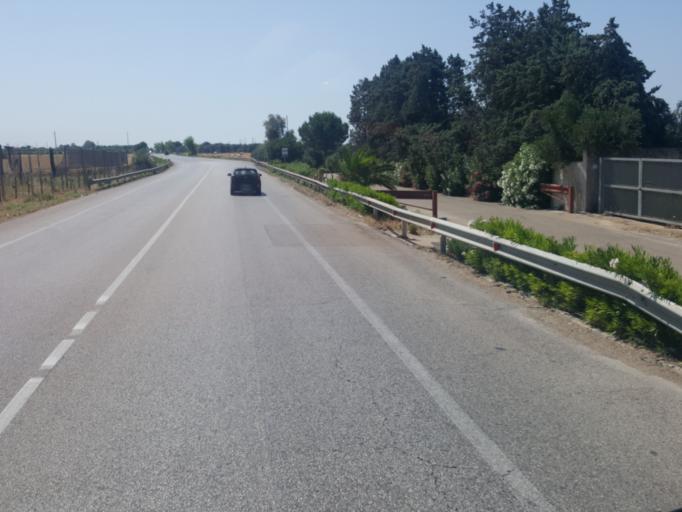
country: IT
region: Apulia
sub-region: Provincia di Taranto
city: Massafra
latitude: 40.5471
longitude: 17.1465
